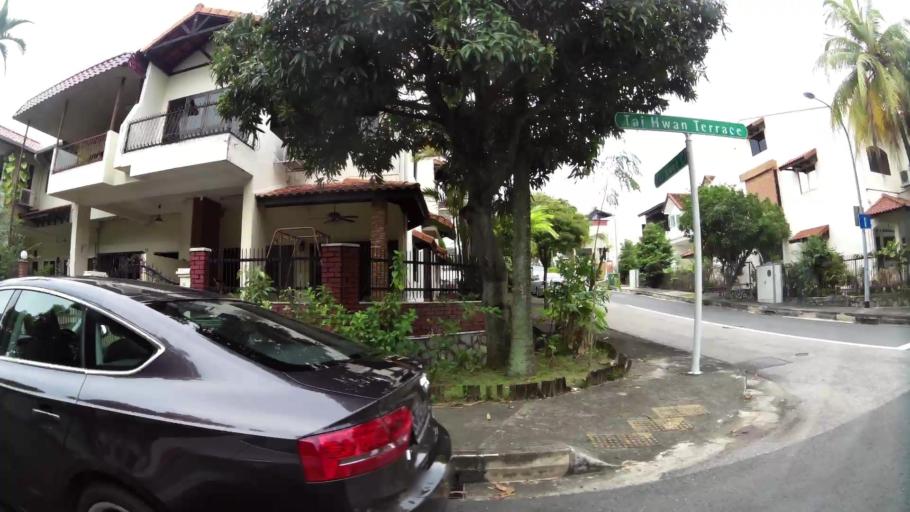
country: SG
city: Singapore
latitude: 1.3570
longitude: 103.8601
